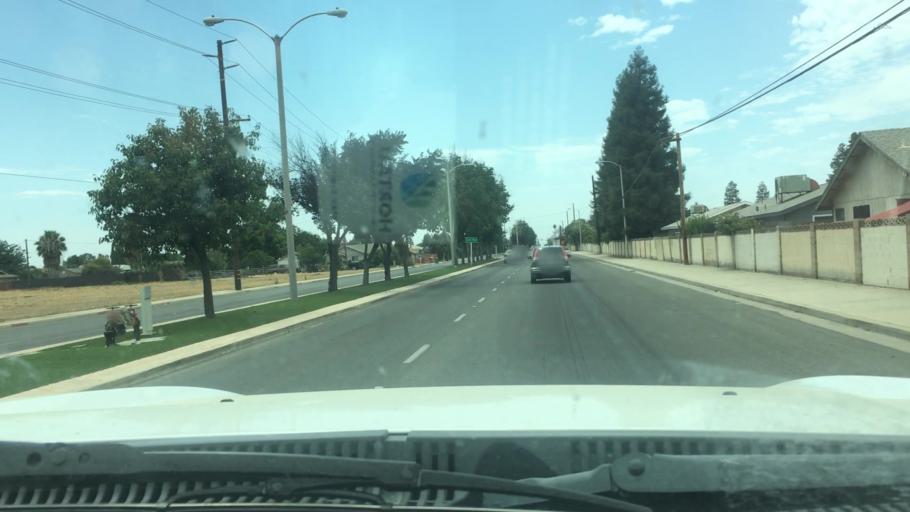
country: US
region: California
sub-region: Tulare County
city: Porterville
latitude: 36.0658
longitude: -119.0641
